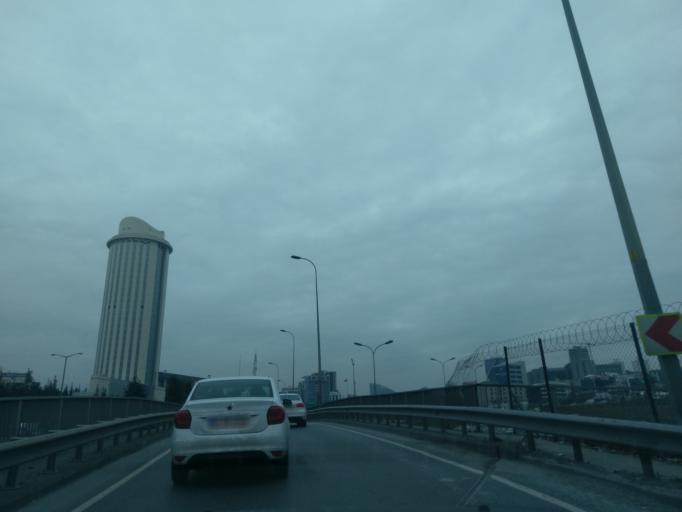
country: TR
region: Istanbul
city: Mahmutbey
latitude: 41.0624
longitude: 28.8206
